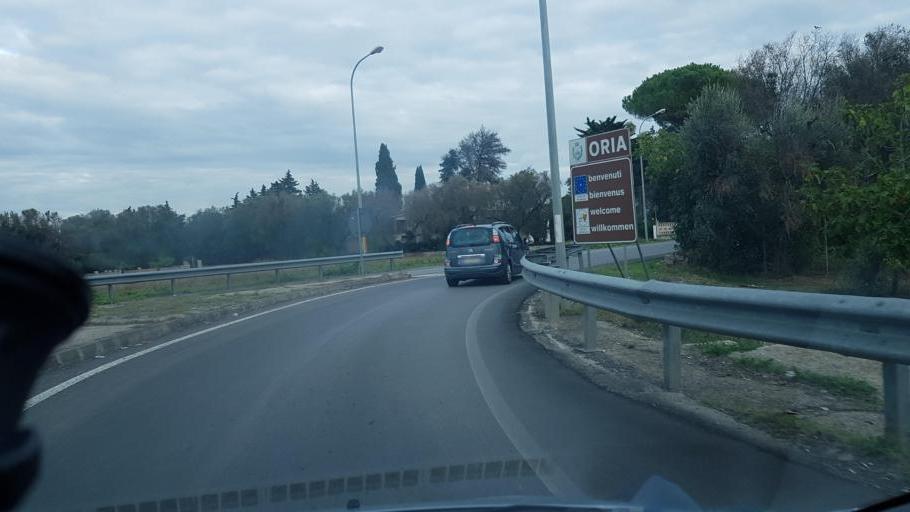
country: IT
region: Apulia
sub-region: Provincia di Brindisi
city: Oria
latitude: 40.5051
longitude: 17.6303
